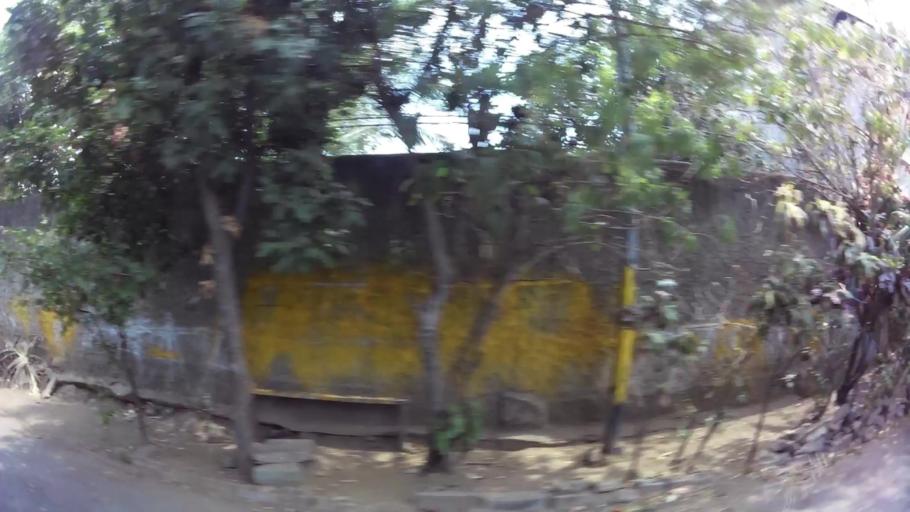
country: NI
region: Managua
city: Ciudad Sandino
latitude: 12.1267
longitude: -86.3089
